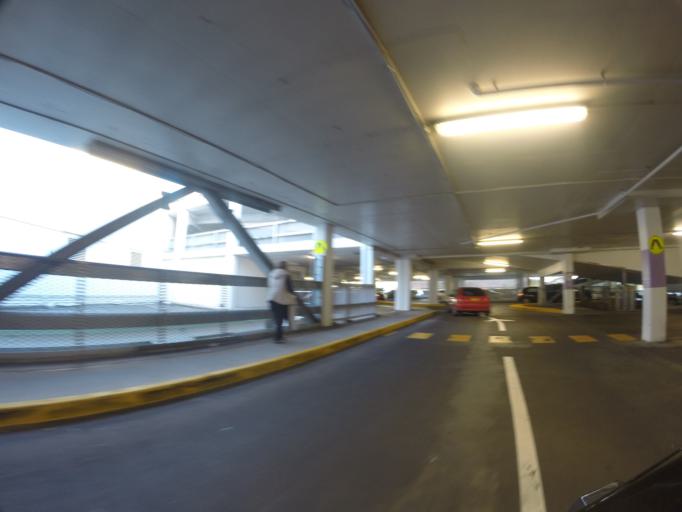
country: AU
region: New South Wales
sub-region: Sutherland Shire
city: Miranda
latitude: -34.0353
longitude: 151.0989
